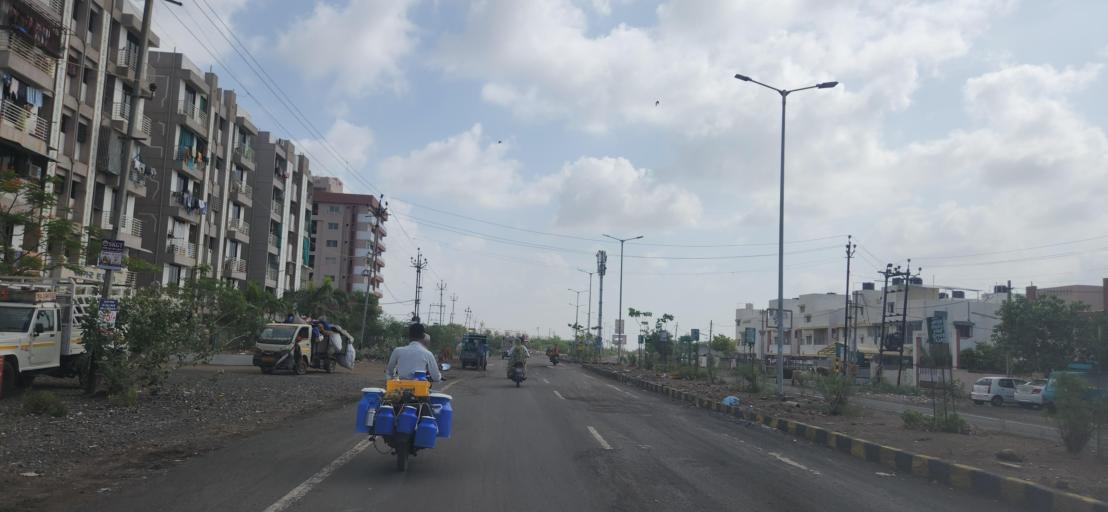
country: IN
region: Gujarat
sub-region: Bhavnagar
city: Bhavnagar
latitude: 21.7566
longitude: 72.1731
